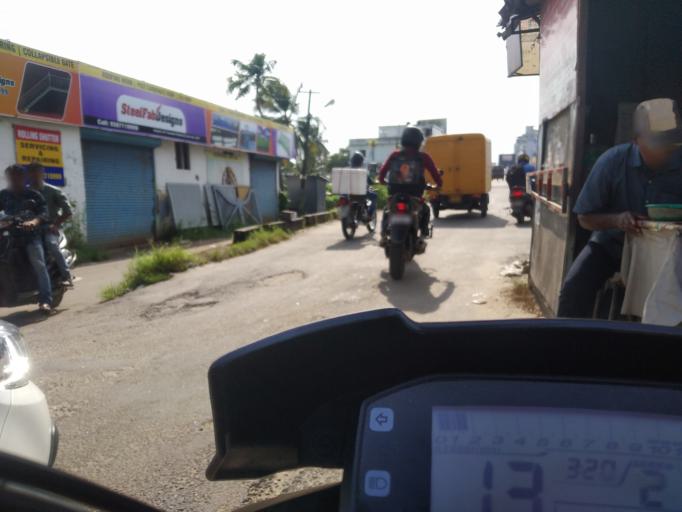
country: IN
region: Kerala
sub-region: Ernakulam
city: Cochin
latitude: 9.9829
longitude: 76.2907
